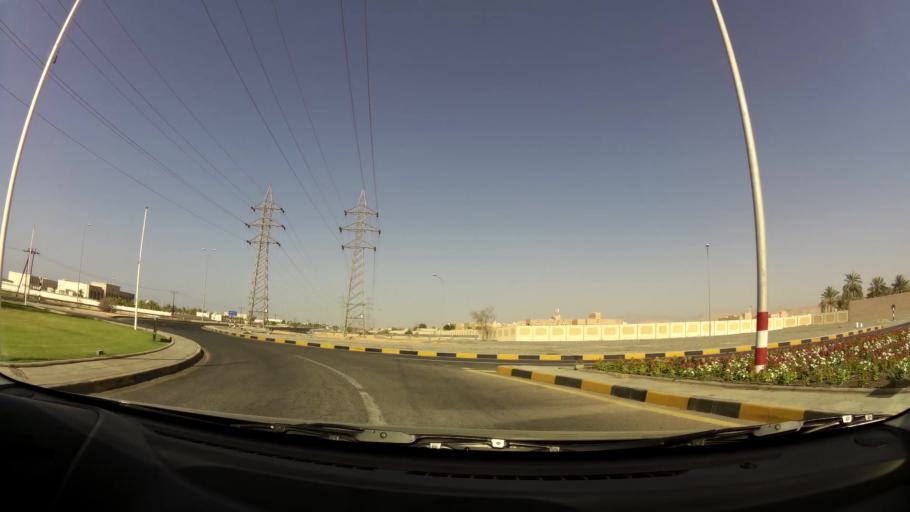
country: OM
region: Muhafazat Masqat
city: As Sib al Jadidah
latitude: 23.5814
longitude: 58.2525
